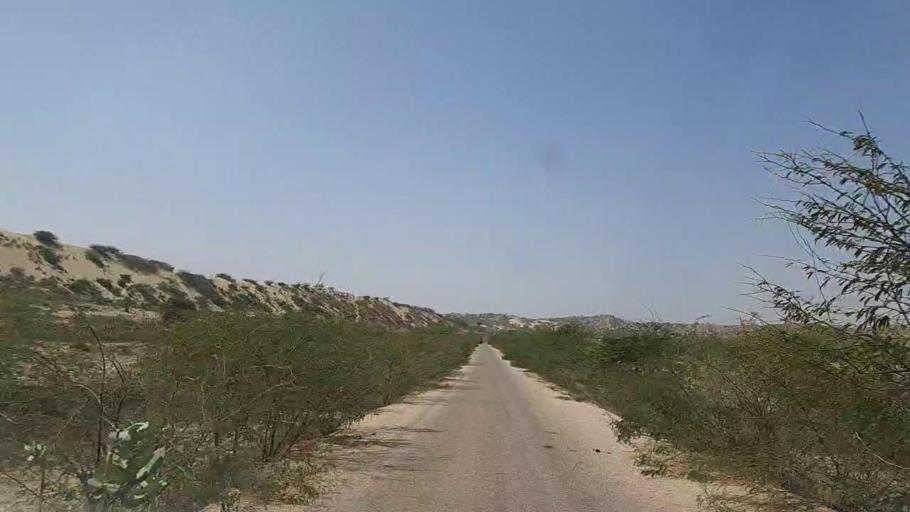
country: PK
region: Sindh
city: Diplo
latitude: 24.5273
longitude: 69.3732
